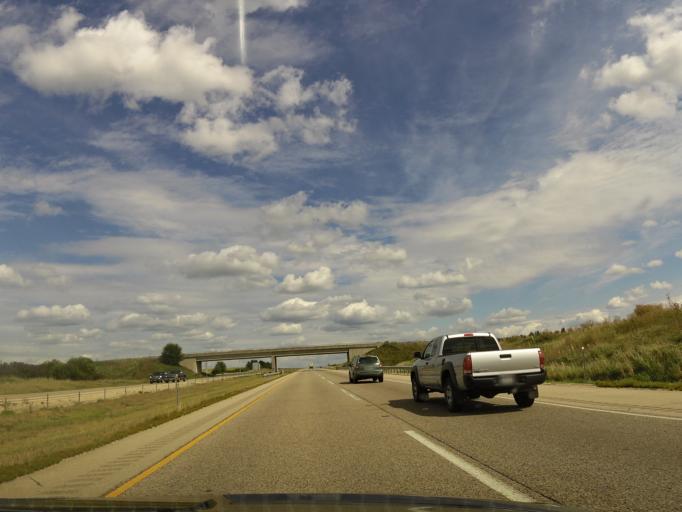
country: US
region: Illinois
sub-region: Ogle County
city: Rochelle
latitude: 41.9053
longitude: -88.9823
